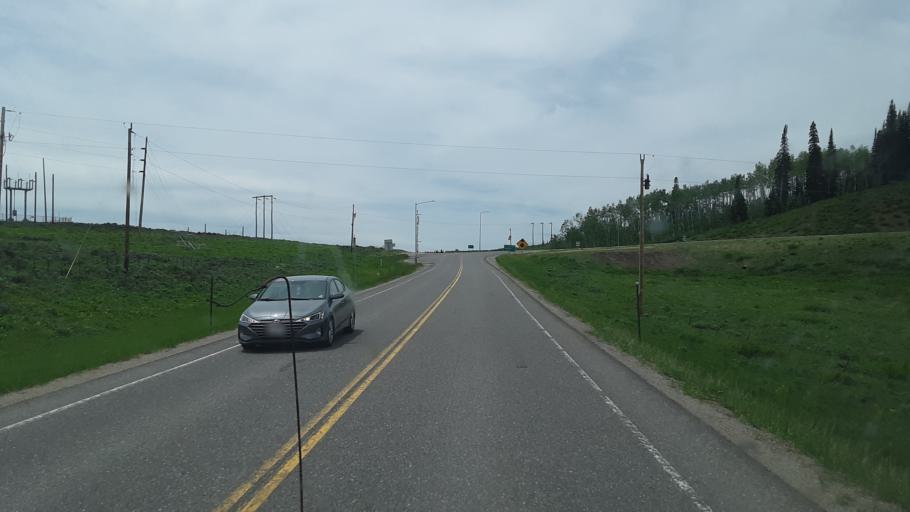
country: US
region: Colorado
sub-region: Routt County
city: Steamboat Springs
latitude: 40.3818
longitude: -106.5778
